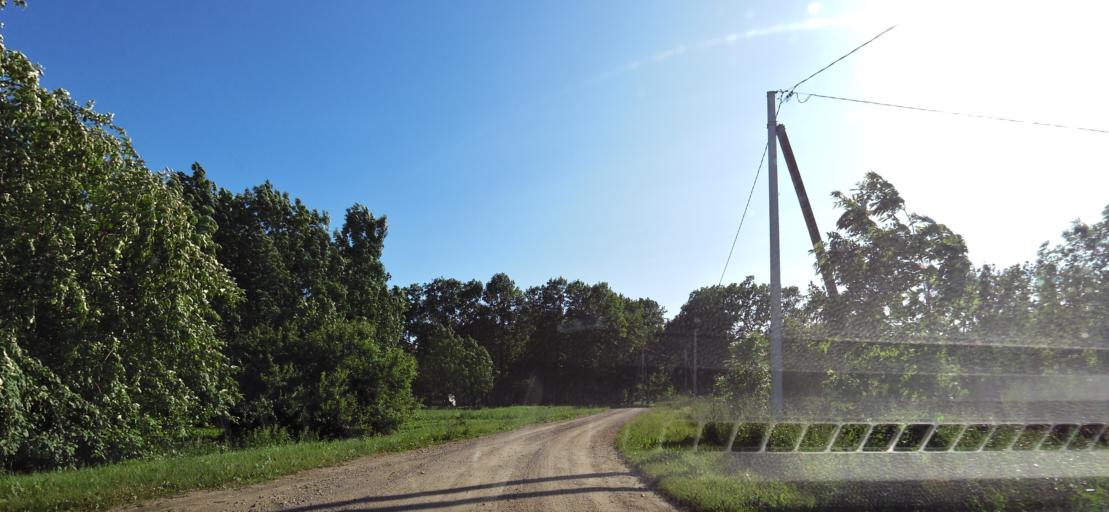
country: LT
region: Panevezys
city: Pasvalys
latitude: 56.1362
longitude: 24.5029
